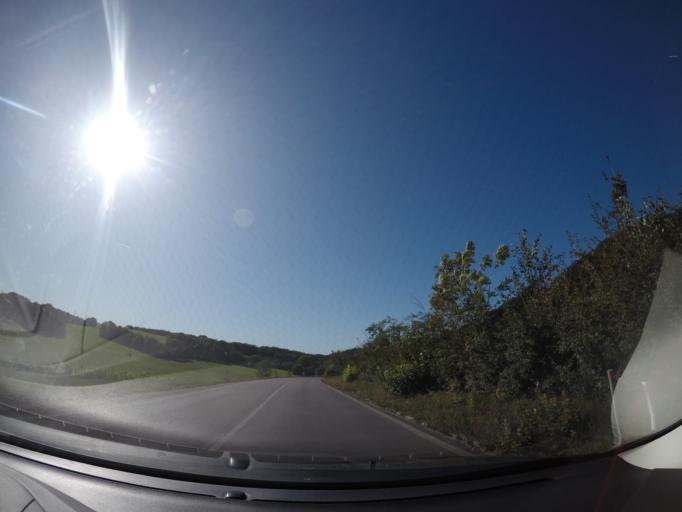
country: AT
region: Lower Austria
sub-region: Politischer Bezirk Modling
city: Laab im Walde
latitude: 48.1594
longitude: 16.1510
